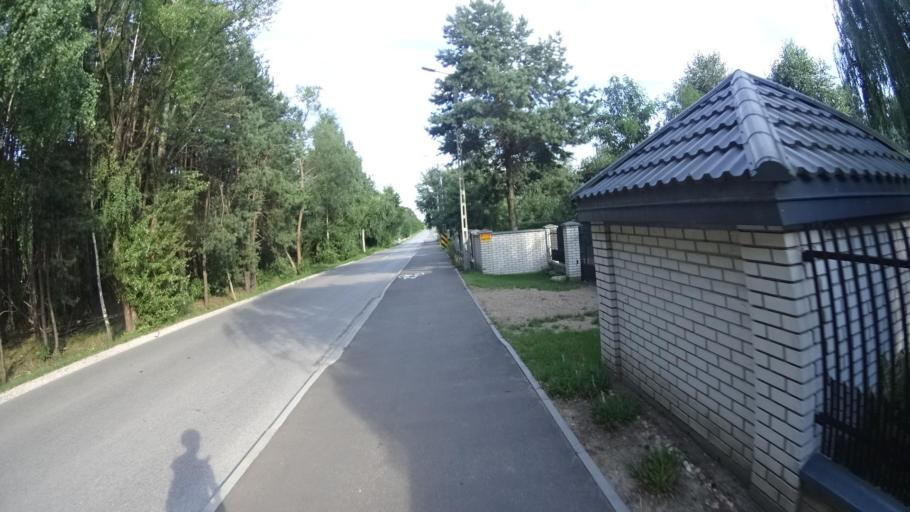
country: PL
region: Masovian Voivodeship
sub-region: Powiat piaseczynski
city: Tarczyn
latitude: 52.0169
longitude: 20.7940
